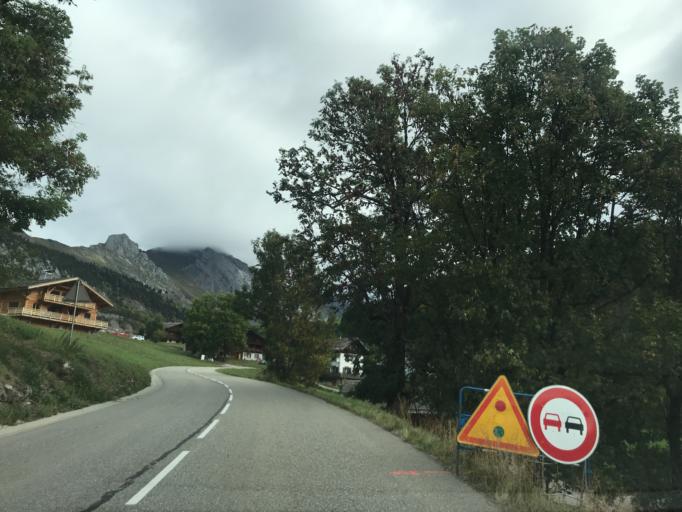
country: FR
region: Rhone-Alpes
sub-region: Departement de la Haute-Savoie
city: Le Grand-Bornand
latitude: 45.9552
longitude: 6.4386
